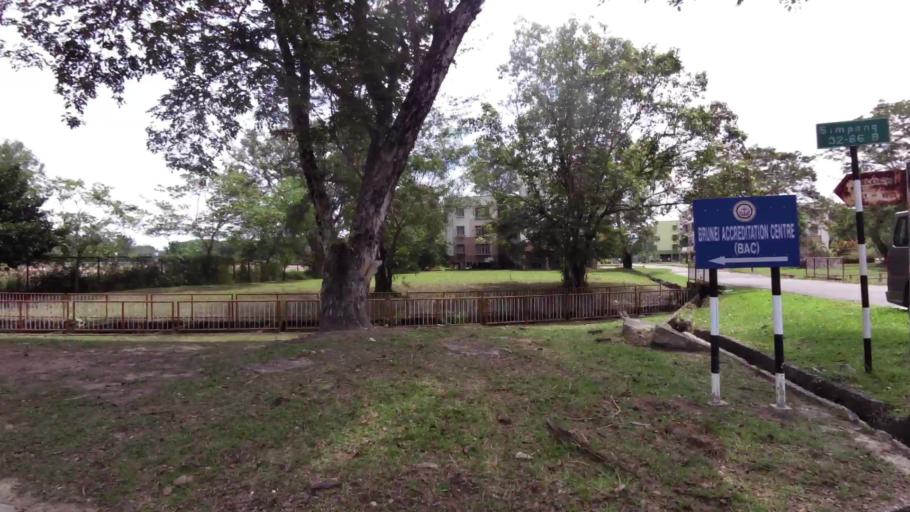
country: BN
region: Brunei and Muara
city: Bandar Seri Begawan
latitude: 4.9329
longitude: 114.9434
